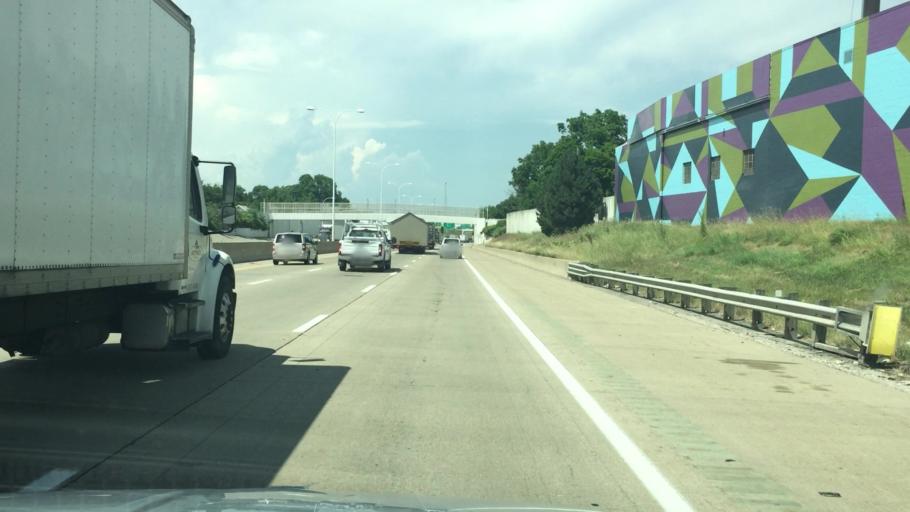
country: US
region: Ohio
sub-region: Lucas County
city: Toledo
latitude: 41.6814
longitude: -83.5156
